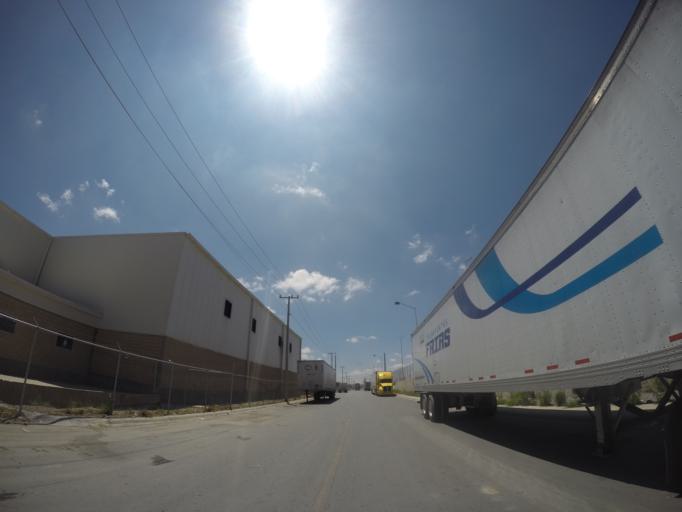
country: MX
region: San Luis Potosi
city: La Pila
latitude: 21.9747
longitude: -100.8784
